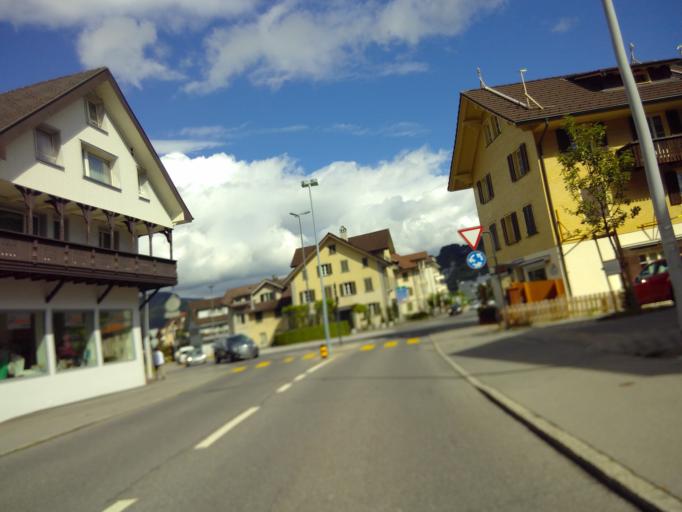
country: CH
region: Nidwalden
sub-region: Nidwalden
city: Stans
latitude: 46.9594
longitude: 8.3624
